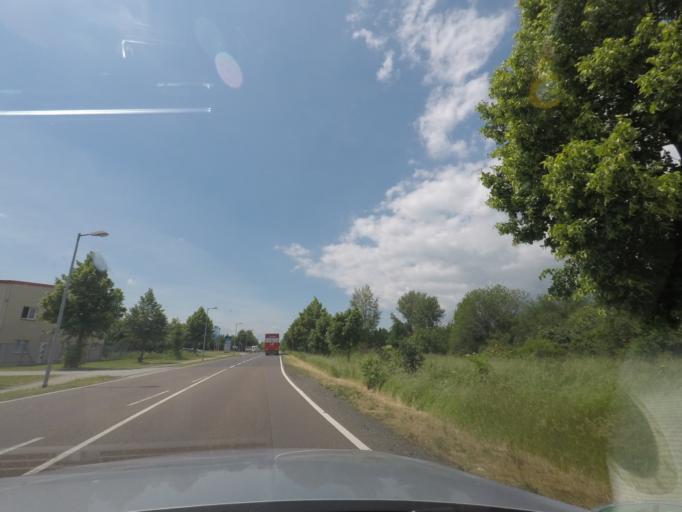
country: DE
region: Saxony
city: Markranstadt
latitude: 51.3148
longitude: 12.2277
